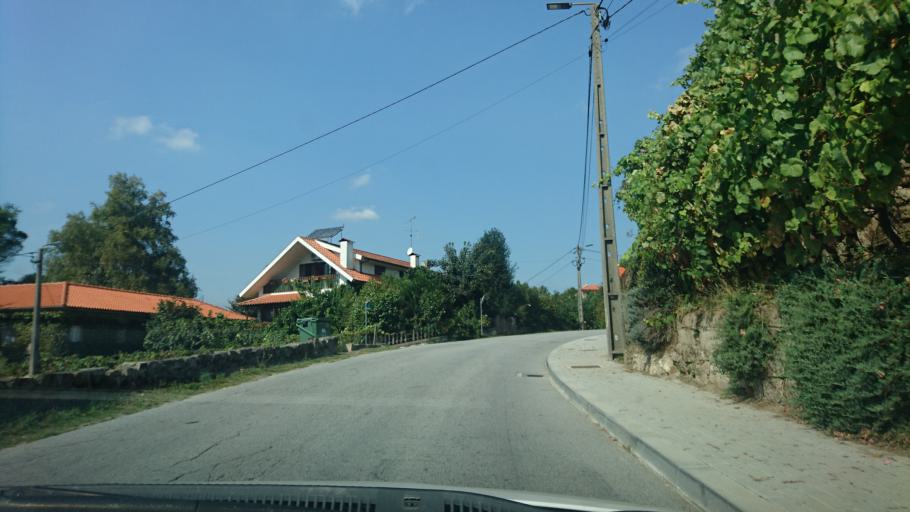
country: PT
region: Vila Real
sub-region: Mondim de Basto
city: Mondim de Basto
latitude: 41.4138
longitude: -7.9489
